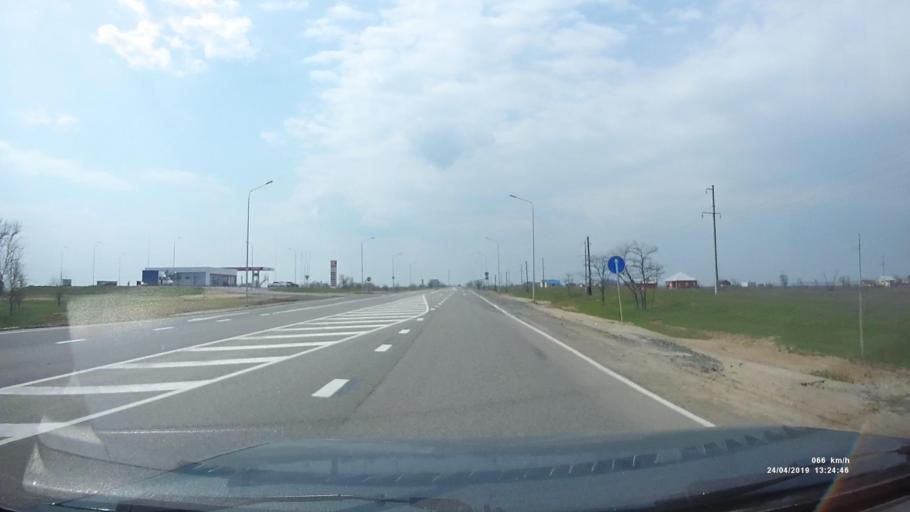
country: RU
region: Kalmykiya
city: Elista
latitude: 46.2852
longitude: 44.2502
